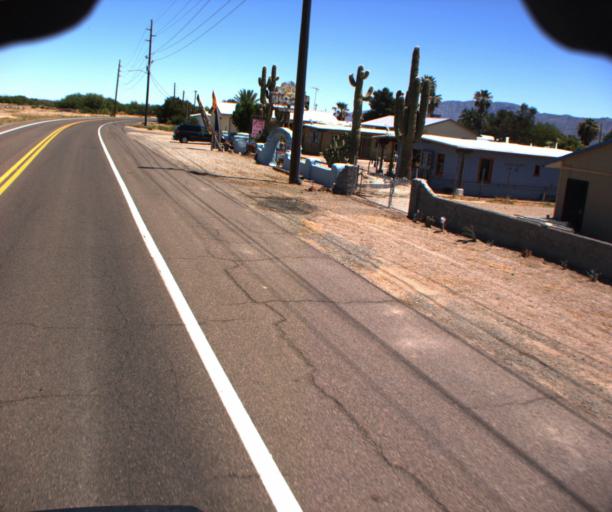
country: US
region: Arizona
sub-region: La Paz County
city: Salome
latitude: 33.8238
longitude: -113.5390
